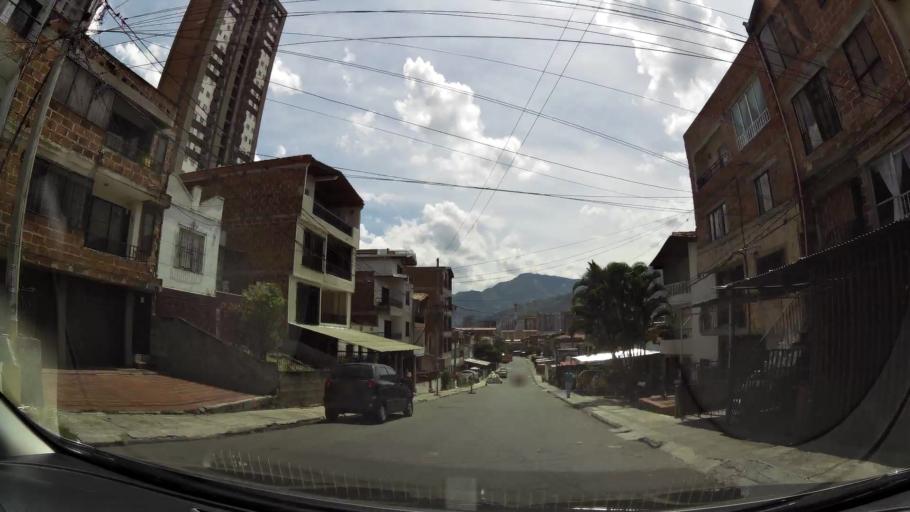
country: CO
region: Antioquia
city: Bello
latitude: 6.3418
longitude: -75.5532
